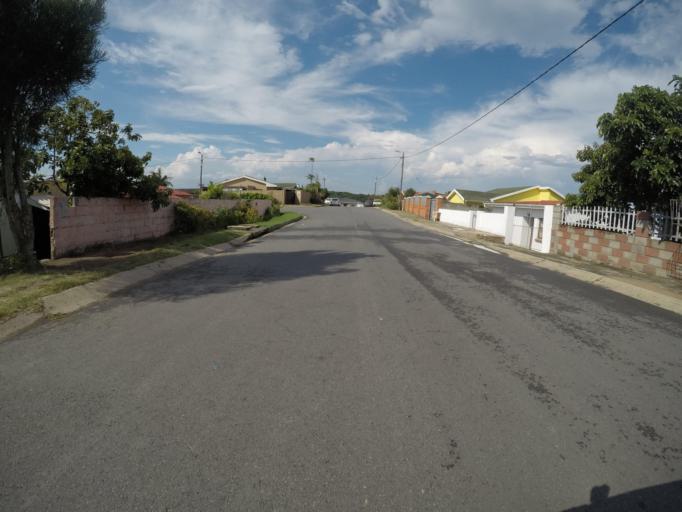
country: ZA
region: Eastern Cape
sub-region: Buffalo City Metropolitan Municipality
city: East London
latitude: -33.0222
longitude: 27.8811
